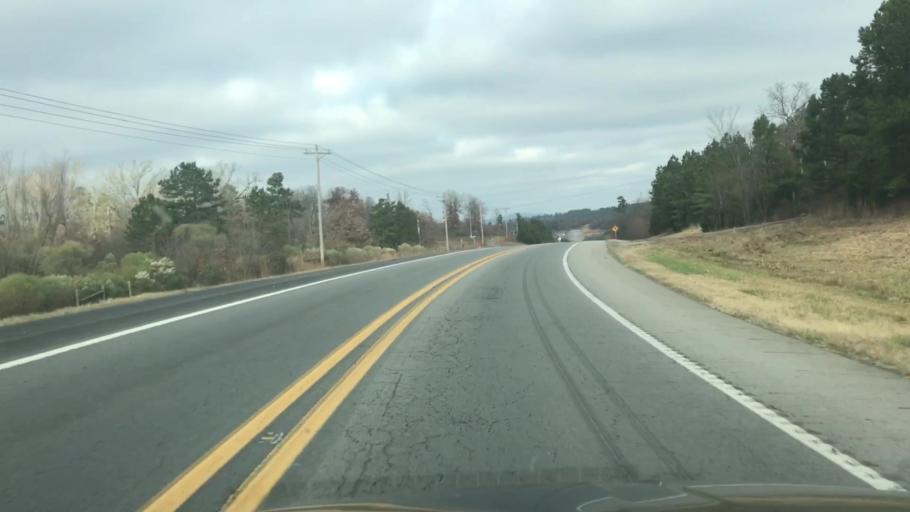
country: US
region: Arkansas
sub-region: Scott County
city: Waldron
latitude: 34.8402
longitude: -94.0530
